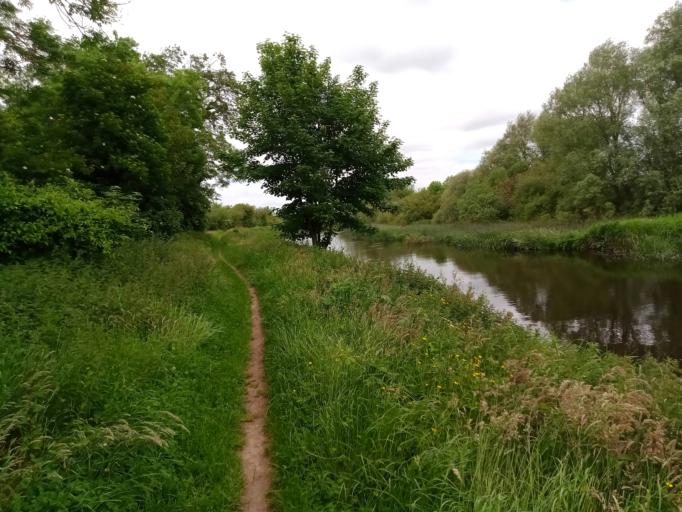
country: IE
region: Leinster
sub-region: County Carlow
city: Carlow
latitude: 52.8013
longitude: -6.9639
